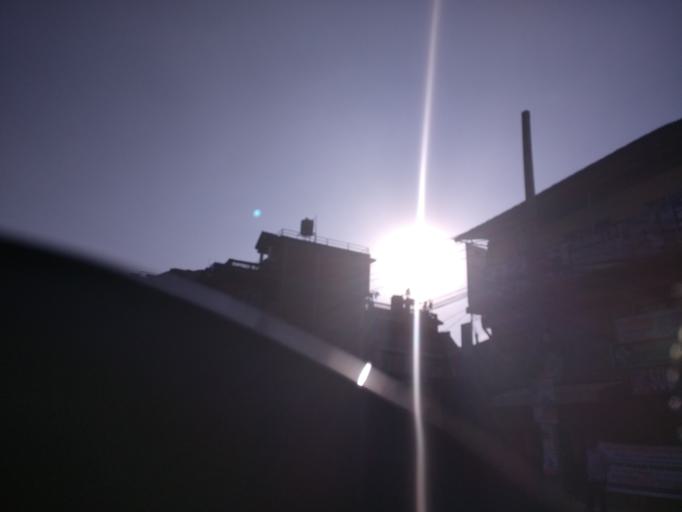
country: NP
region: Central Region
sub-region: Bagmati Zone
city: Patan
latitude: 27.6572
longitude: 85.3221
